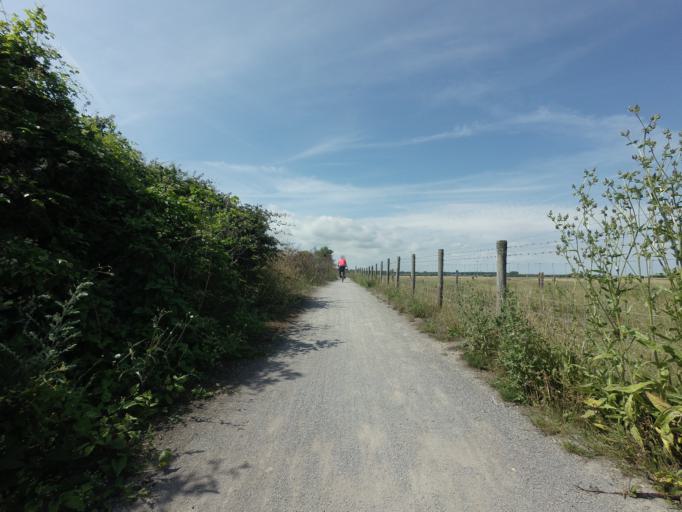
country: GB
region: England
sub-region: East Sussex
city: Rye
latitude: 50.9453
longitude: 0.7611
